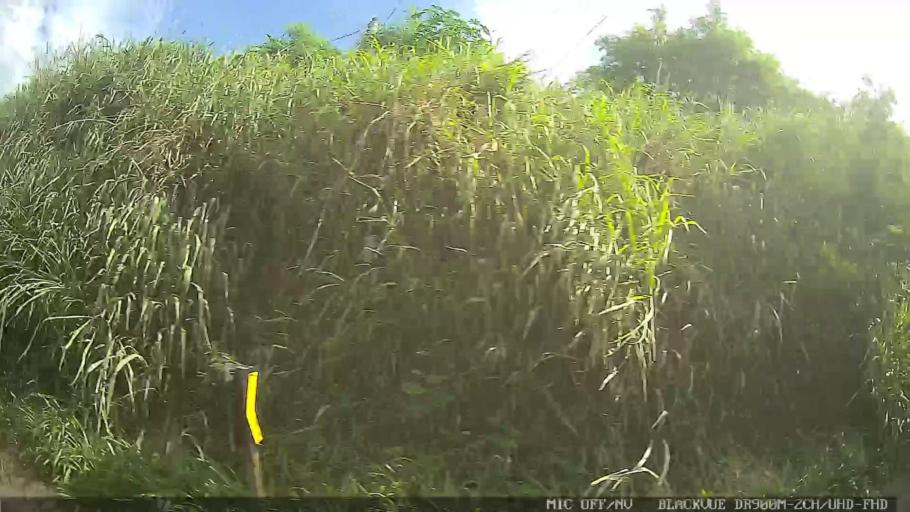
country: BR
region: Sao Paulo
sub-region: Laranjal Paulista
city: Laranjal Paulista
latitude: -23.0443
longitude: -47.8449
